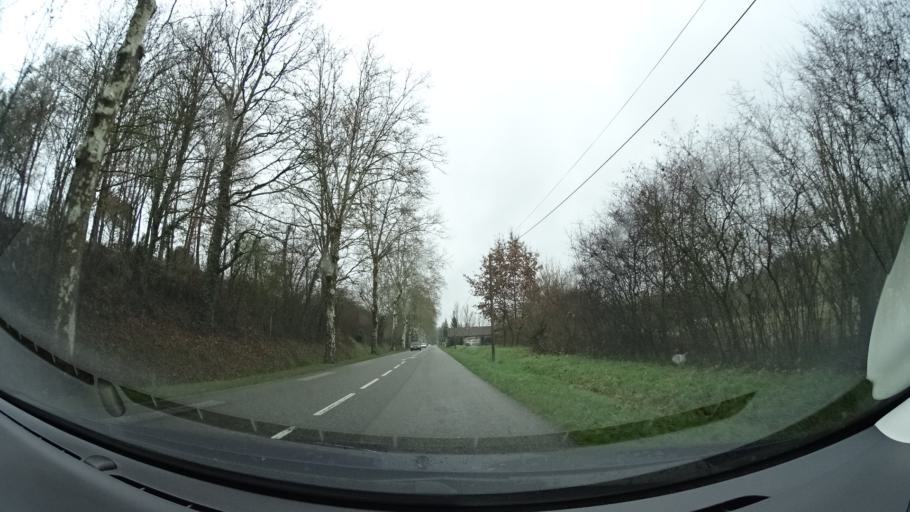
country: FR
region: Midi-Pyrenees
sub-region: Departement du Tarn-et-Garonne
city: Moissac
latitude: 44.1382
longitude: 1.1008
